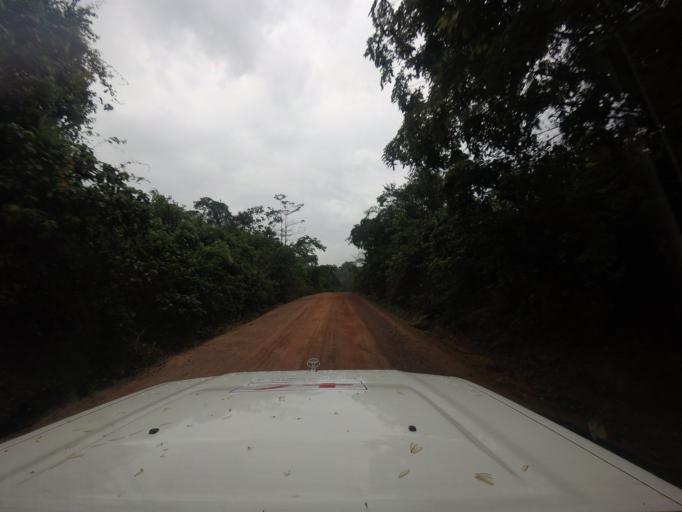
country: LR
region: Lofa
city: Voinjama
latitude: 8.3843
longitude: -9.8296
